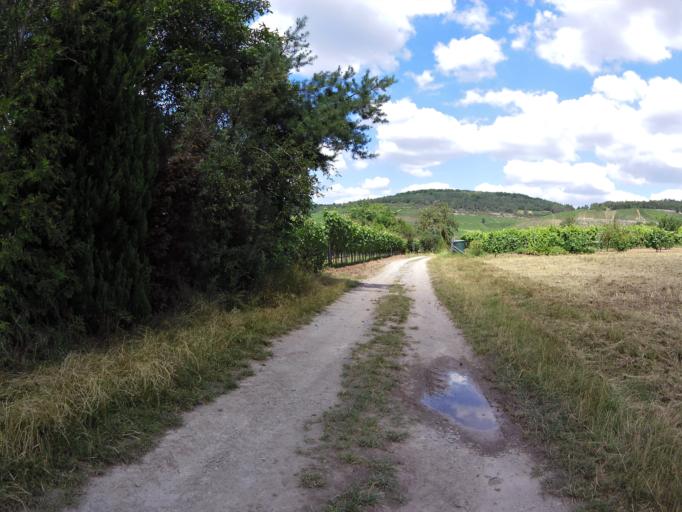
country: DE
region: Bavaria
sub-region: Regierungsbezirk Unterfranken
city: Thungersheim
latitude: 49.8818
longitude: 9.8521
